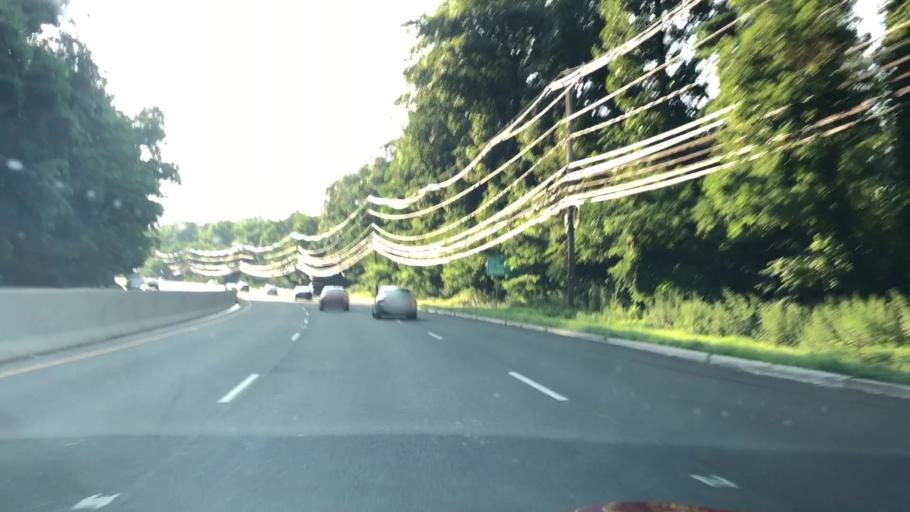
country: US
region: New Jersey
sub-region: Morris County
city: Morris Plains
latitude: 40.8545
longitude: -74.4780
